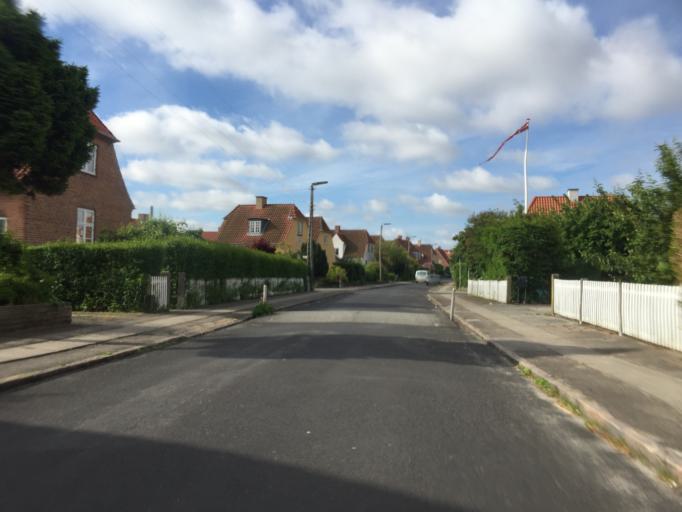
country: DK
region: Capital Region
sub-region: Frederiksberg Kommune
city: Frederiksberg
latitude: 55.6946
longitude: 12.5163
